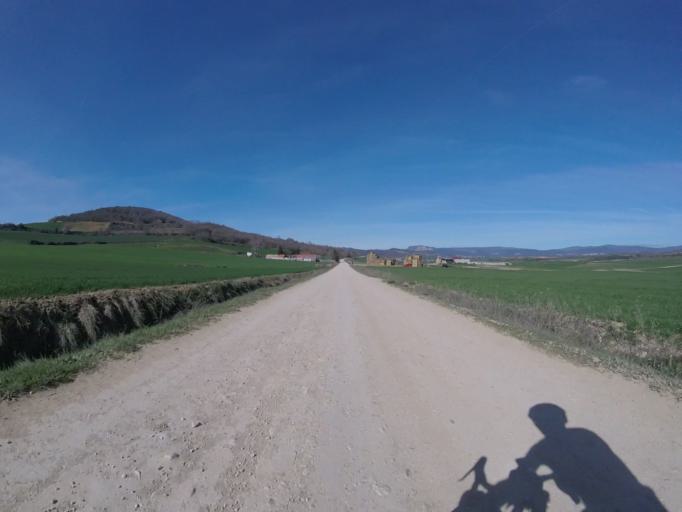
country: ES
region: Navarre
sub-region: Provincia de Navarra
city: Villatuerta
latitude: 42.6511
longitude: -1.9720
